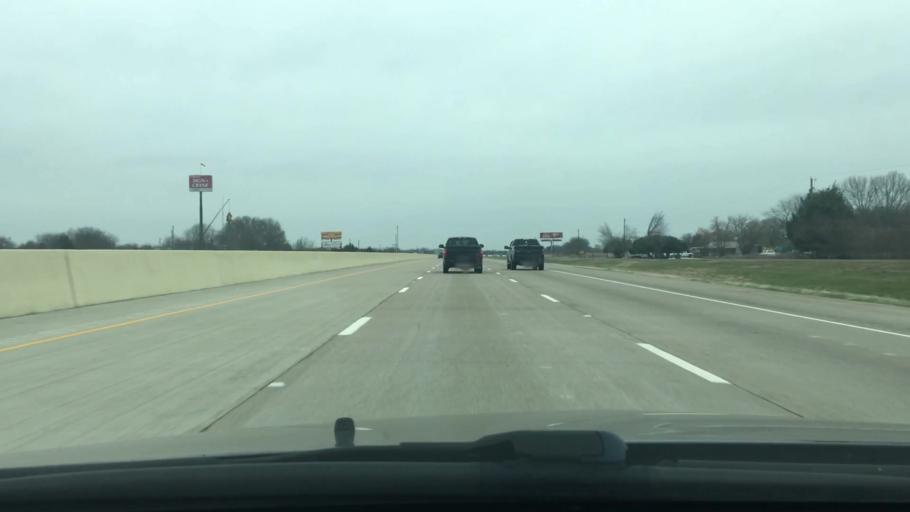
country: US
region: Texas
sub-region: Navarro County
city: Corsicana
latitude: 31.9913
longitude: -96.4268
